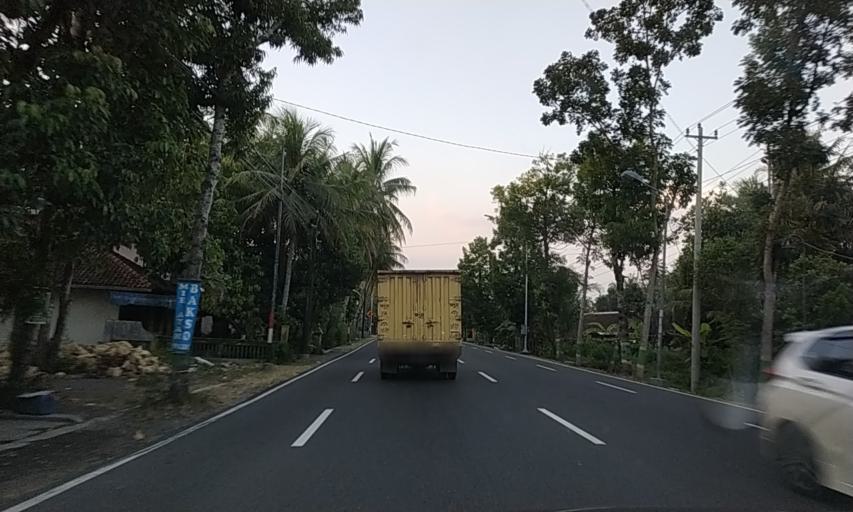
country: ID
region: Daerah Istimewa Yogyakarta
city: Srandakan
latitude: -7.8807
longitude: 110.1321
